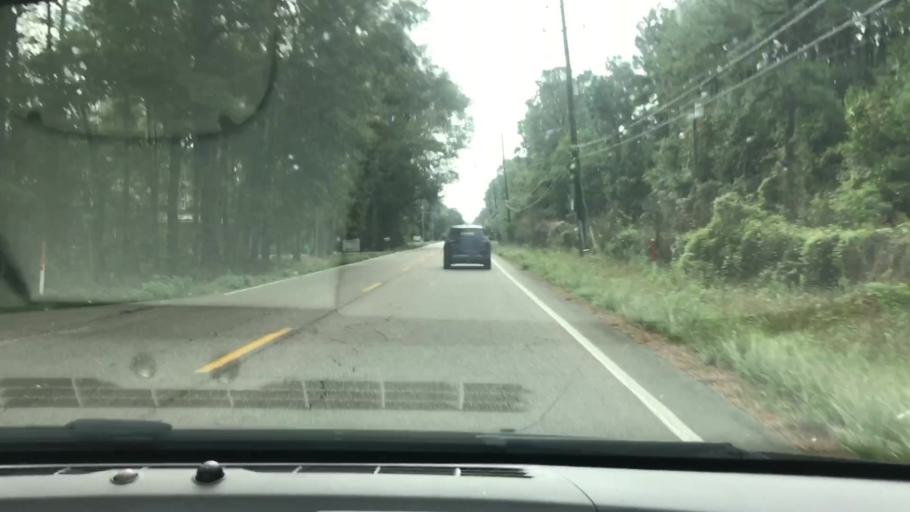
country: US
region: Louisiana
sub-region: Saint Tammany Parish
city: Abita Springs
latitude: 30.4675
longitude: -90.0407
